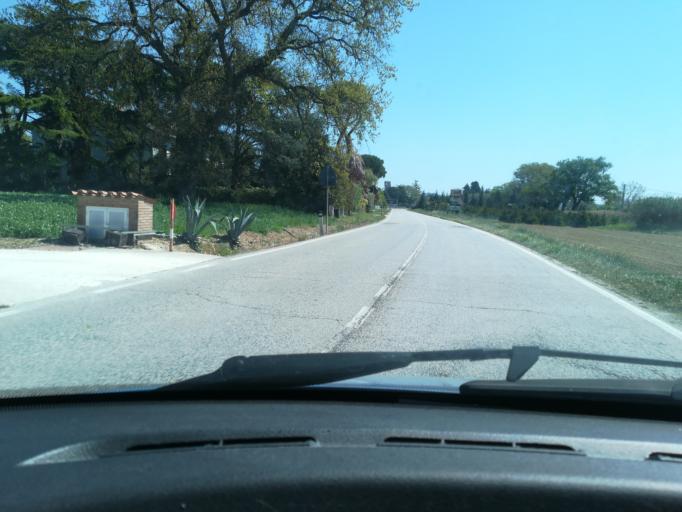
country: IT
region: The Marches
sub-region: Provincia di Ancona
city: Castelfidardo
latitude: 43.4521
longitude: 13.5301
